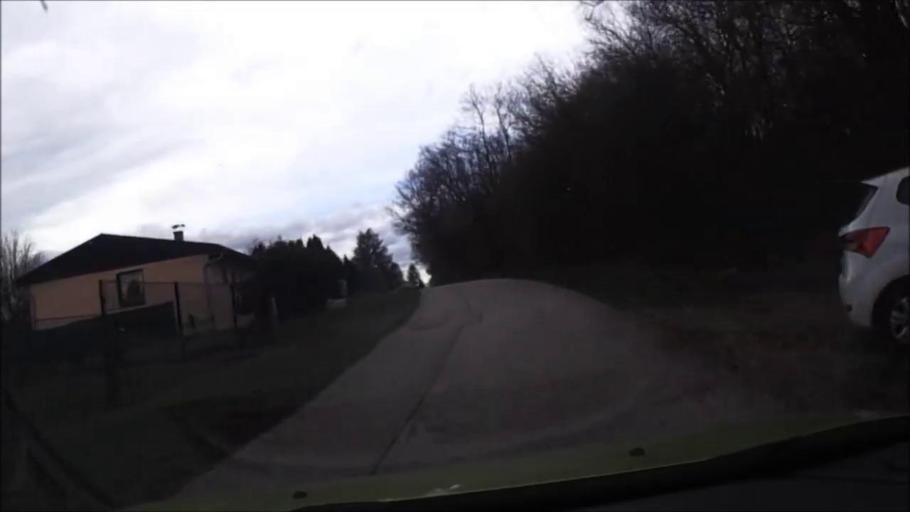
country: AT
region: Burgenland
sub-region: Eisenstadt-Umgebung
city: Loretto
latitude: 47.8985
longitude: 16.5202
